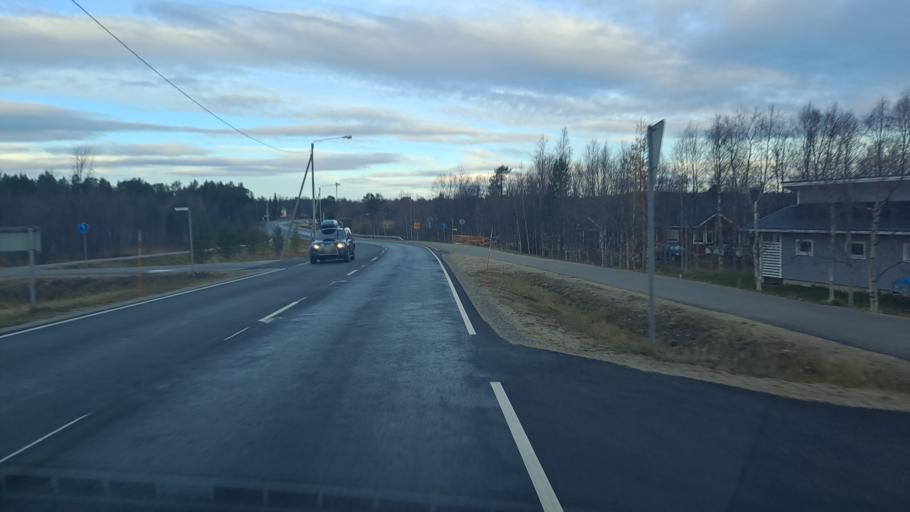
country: FI
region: Lapland
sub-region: Pohjois-Lappi
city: Inari
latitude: 68.9010
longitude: 27.0434
